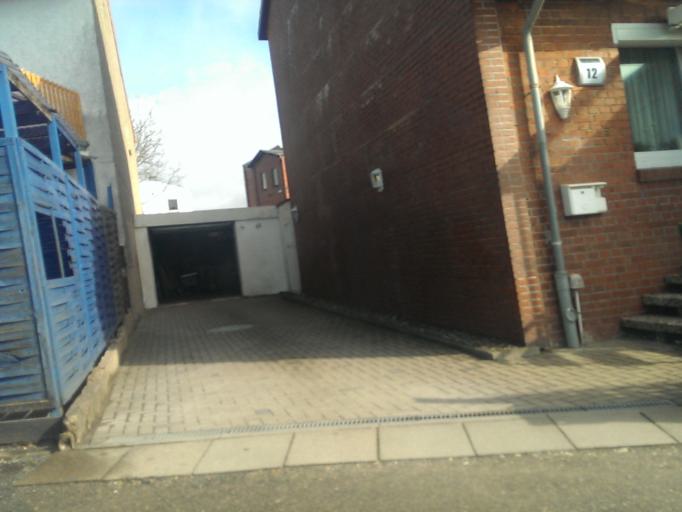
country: DE
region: Lower Saxony
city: Schellerten
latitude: 52.1681
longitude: 10.0570
